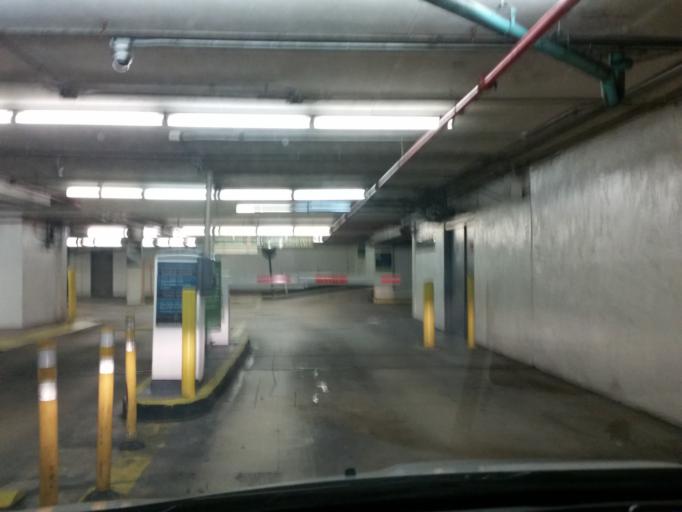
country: US
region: Florida
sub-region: Miami-Dade County
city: Coconut Grove
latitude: 25.7290
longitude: -80.2416
